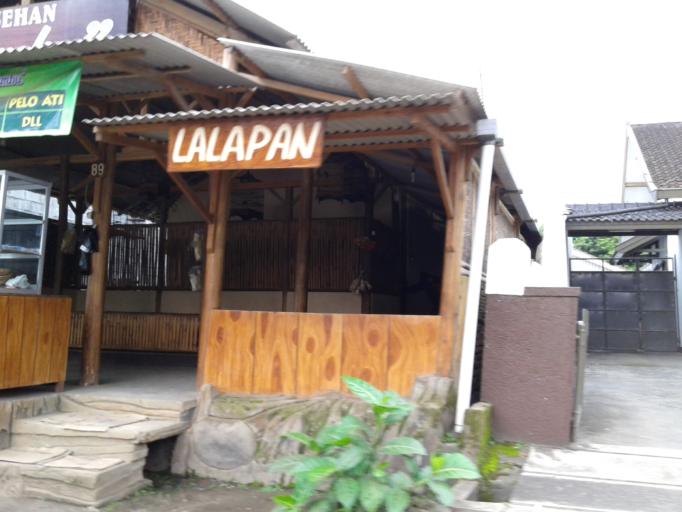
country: ID
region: East Java
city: Singosari
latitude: -7.8678
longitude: 112.6523
